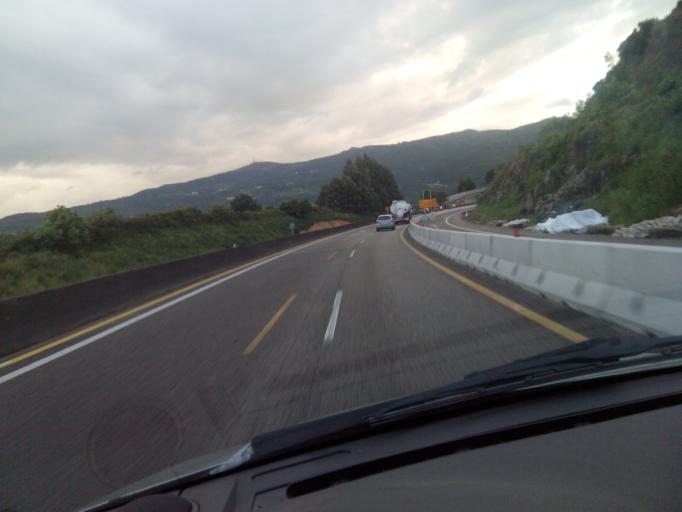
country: ES
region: Galicia
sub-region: Provincia de Pontevedra
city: Redondela
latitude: 42.2737
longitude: -8.6653
